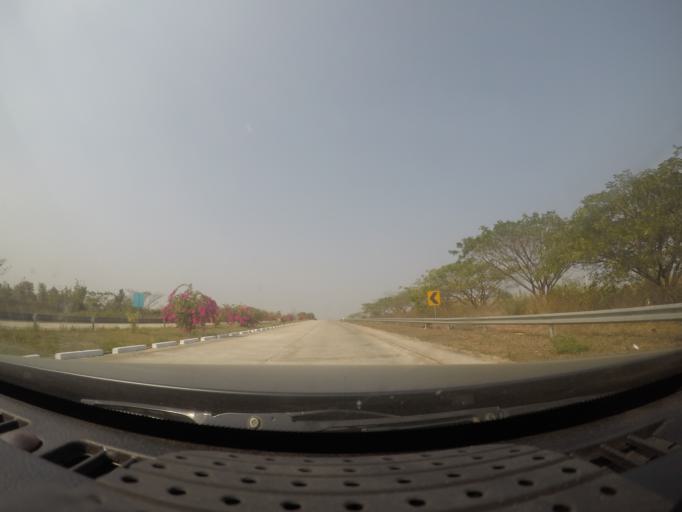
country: MM
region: Mandalay
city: Nay Pyi Taw
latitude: 19.9547
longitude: 95.9902
